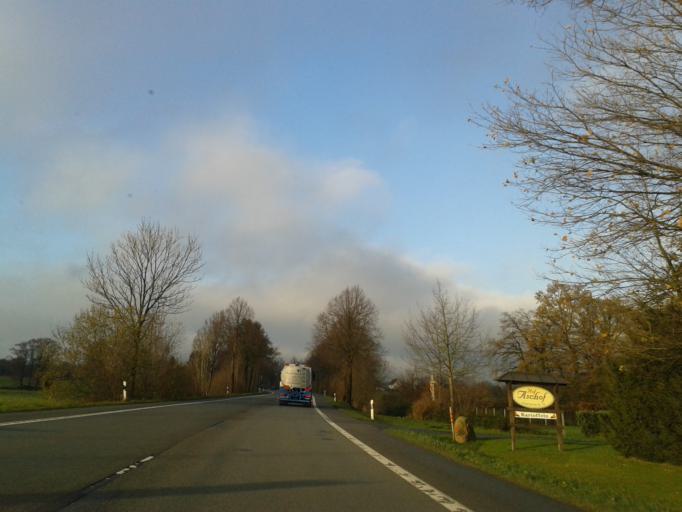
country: DE
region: North Rhine-Westphalia
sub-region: Regierungsbezirk Detmold
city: Oerlinghausen
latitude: 51.8982
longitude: 8.6688
